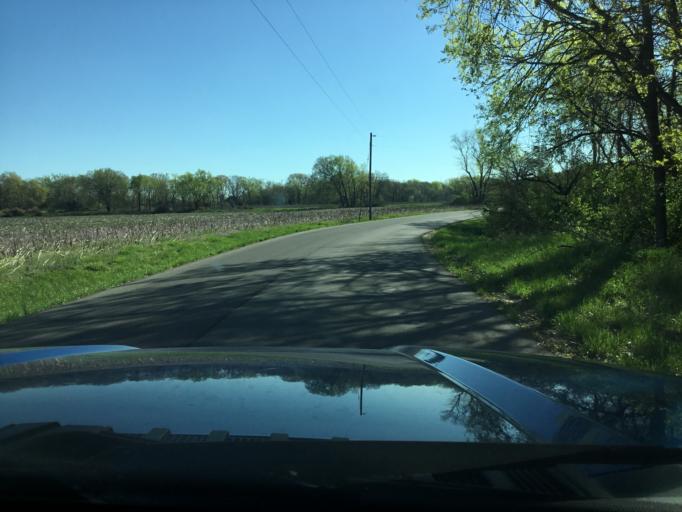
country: US
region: Kansas
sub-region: Douglas County
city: Lawrence
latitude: 38.9940
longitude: -95.3089
